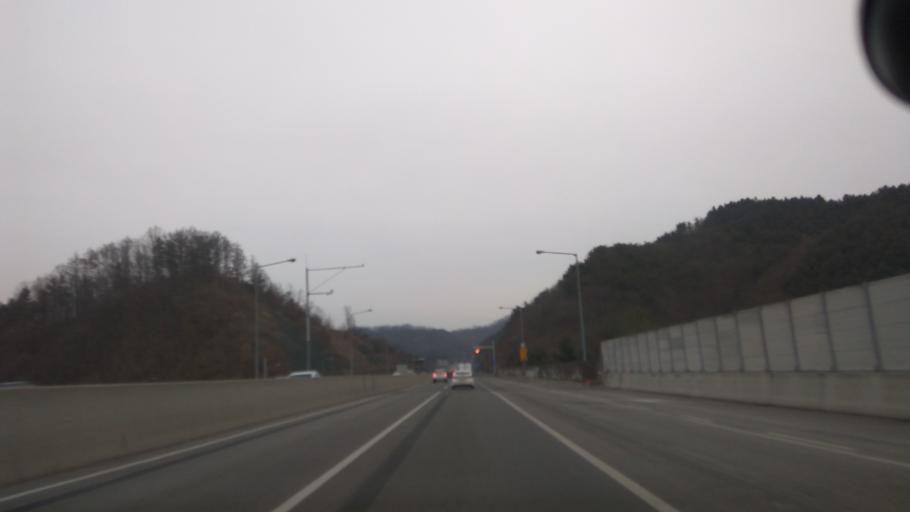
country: KR
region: Gangwon-do
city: Sindong
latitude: 37.7349
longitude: 127.6253
